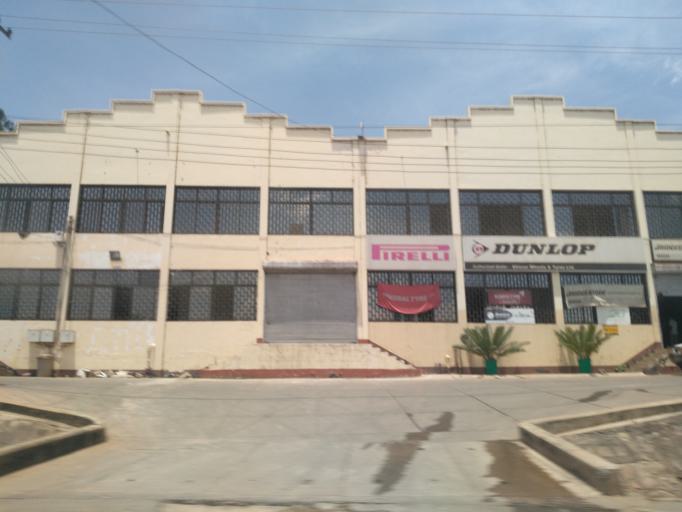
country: TZ
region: Mwanza
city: Mwanza
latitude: -2.5319
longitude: 32.9023
